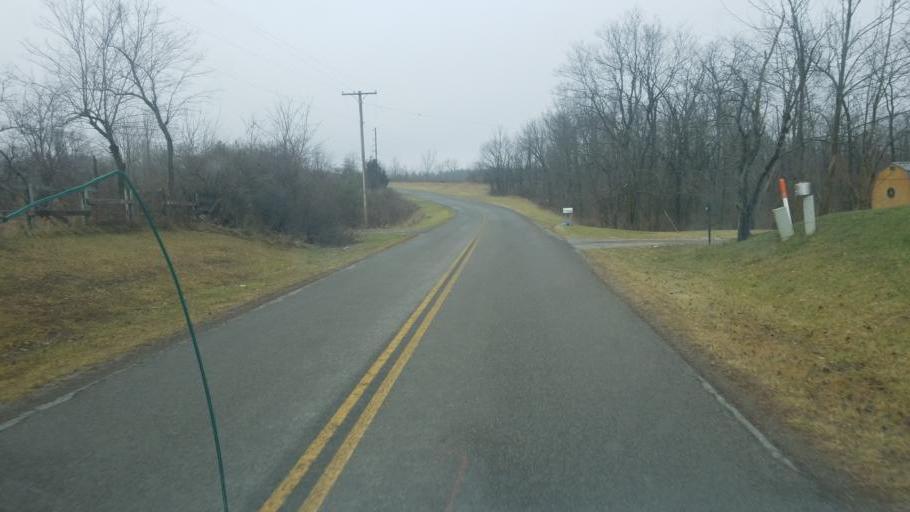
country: US
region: Ohio
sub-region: Champaign County
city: North Lewisburg
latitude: 40.2985
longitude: -83.5780
